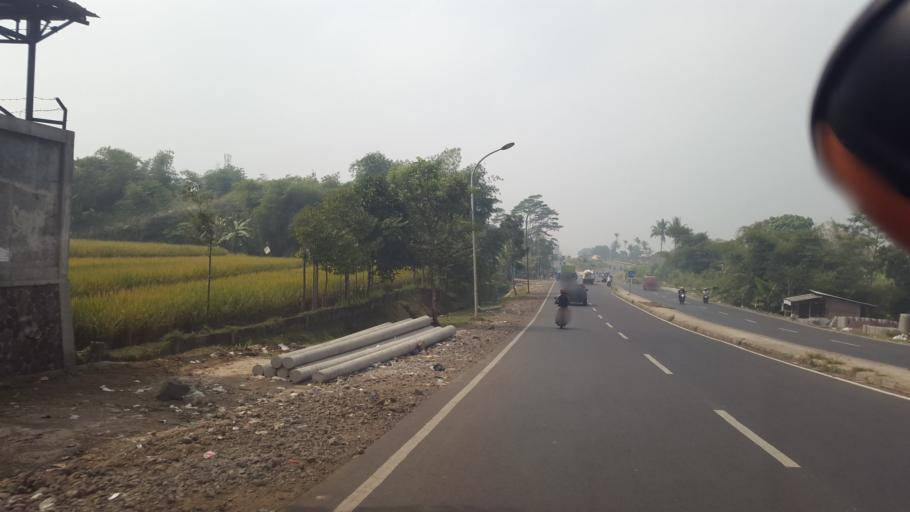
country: ID
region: West Java
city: Sukabumi
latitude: -6.9141
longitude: 106.8809
